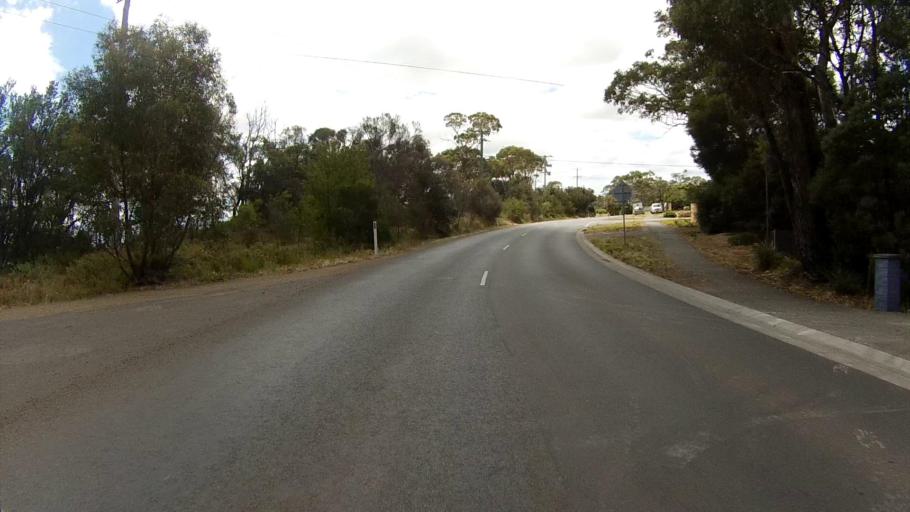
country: AU
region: Tasmania
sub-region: Sorell
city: Sorell
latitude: -42.8655
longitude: 147.6117
